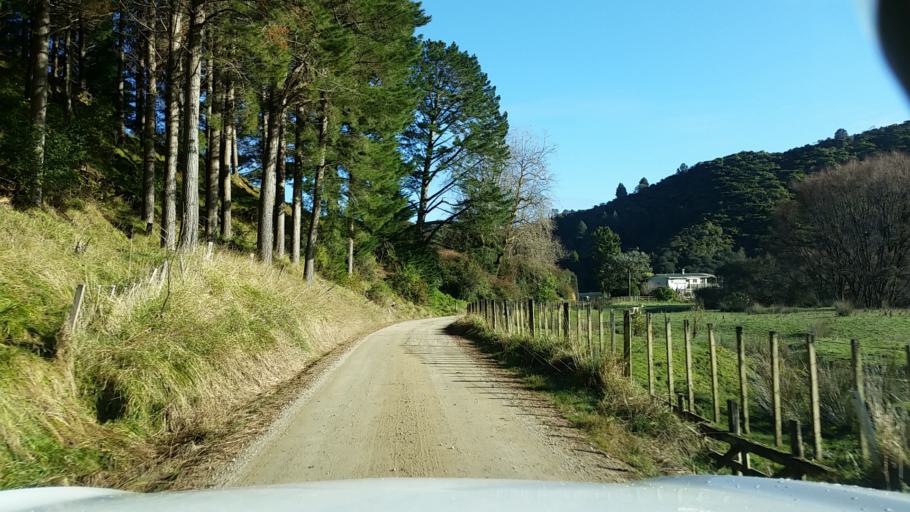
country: NZ
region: Taranaki
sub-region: South Taranaki District
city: Patea
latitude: -39.7001
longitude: 174.7362
